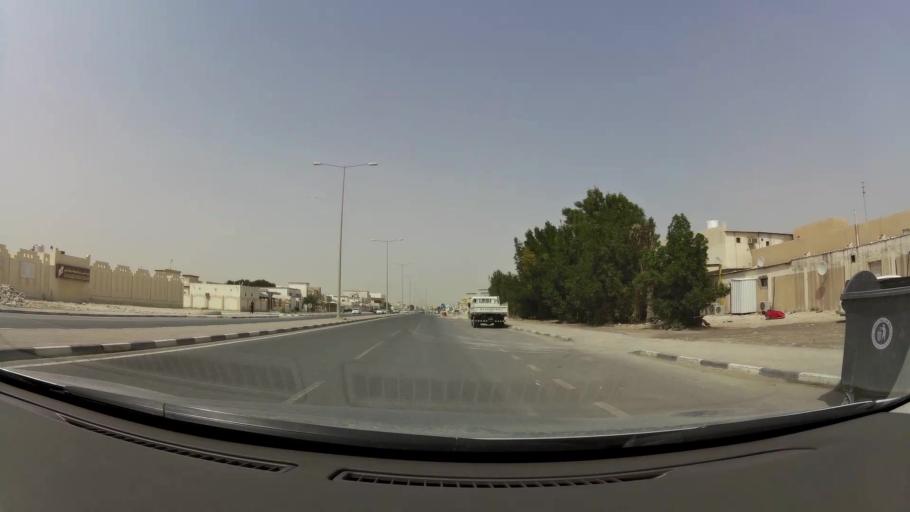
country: QA
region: Baladiyat ar Rayyan
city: Ar Rayyan
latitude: 25.2349
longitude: 51.4204
